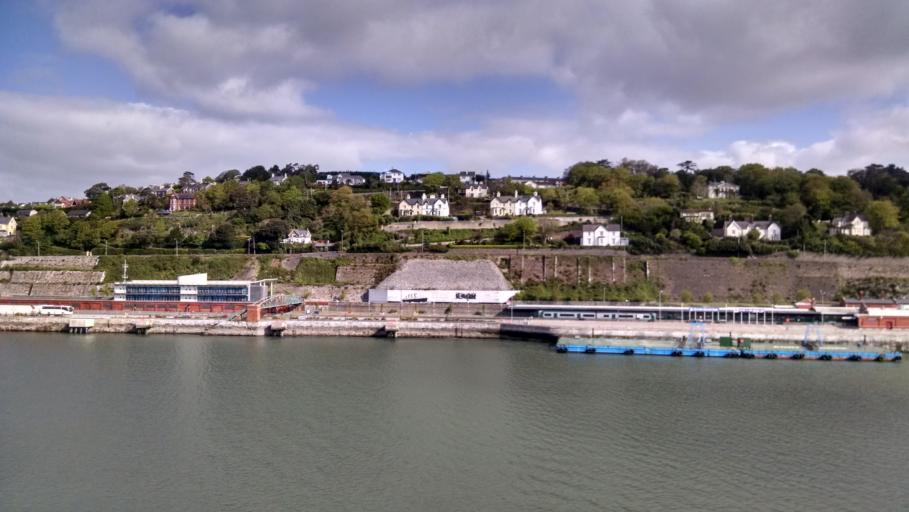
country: IE
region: Munster
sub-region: County Cork
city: Cobh
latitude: 51.8463
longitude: -8.3003
